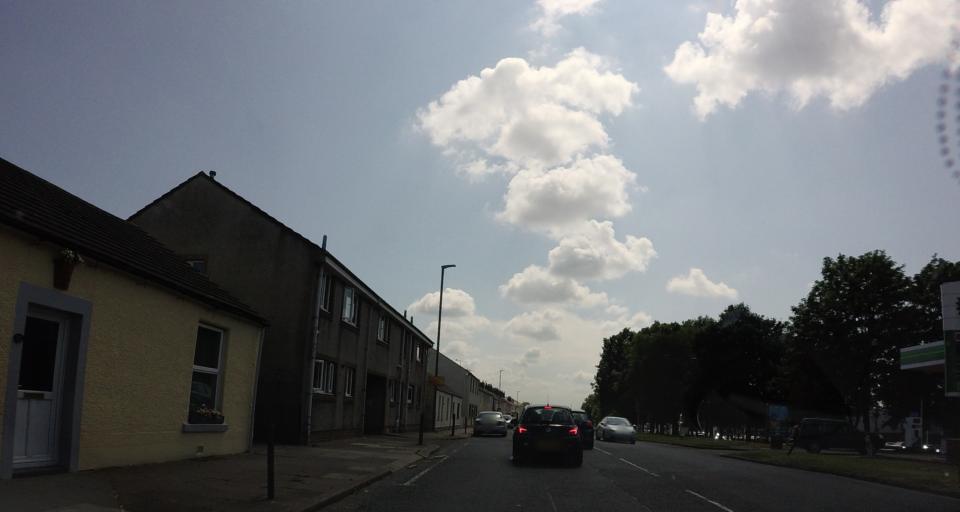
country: GB
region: England
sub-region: Cumbria
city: Carlisle
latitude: 54.9251
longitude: -2.9454
